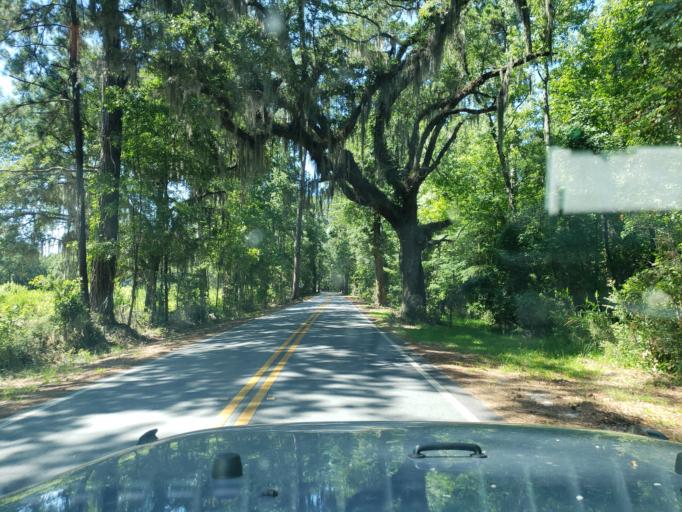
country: US
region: Georgia
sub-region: Chatham County
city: Georgetown
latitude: 31.9633
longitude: -81.2189
